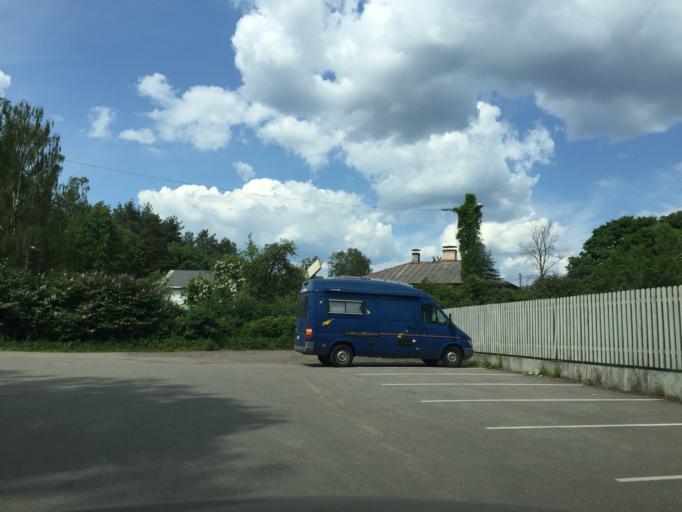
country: LV
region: Riga
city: Bergi
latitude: 56.9950
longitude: 24.2699
